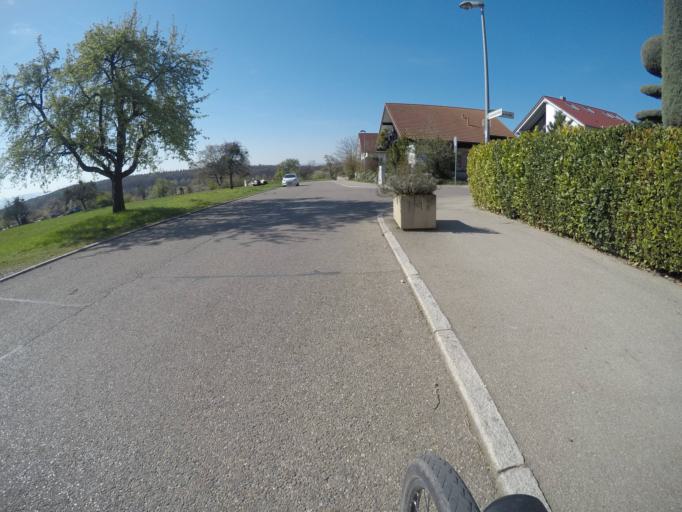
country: DE
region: Baden-Wuerttemberg
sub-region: Regierungsbezirk Stuttgart
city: Filderstadt
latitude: 48.6488
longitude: 9.1927
